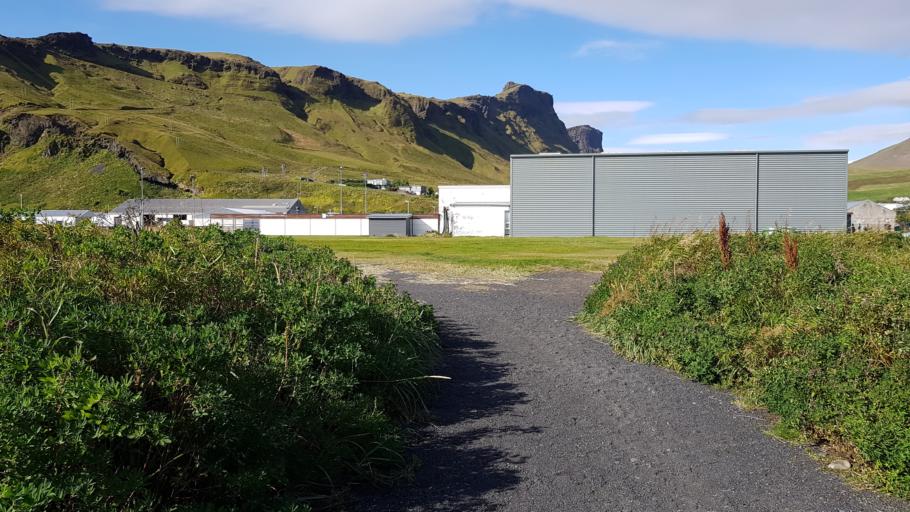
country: IS
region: South
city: Vestmannaeyjar
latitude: 63.4163
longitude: -19.0071
